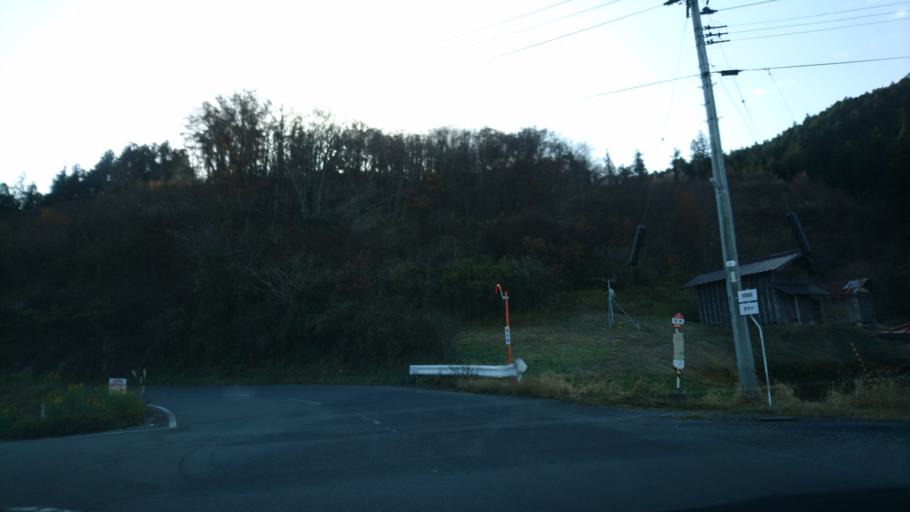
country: JP
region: Iwate
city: Ichinoseki
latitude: 38.8945
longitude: 141.2776
